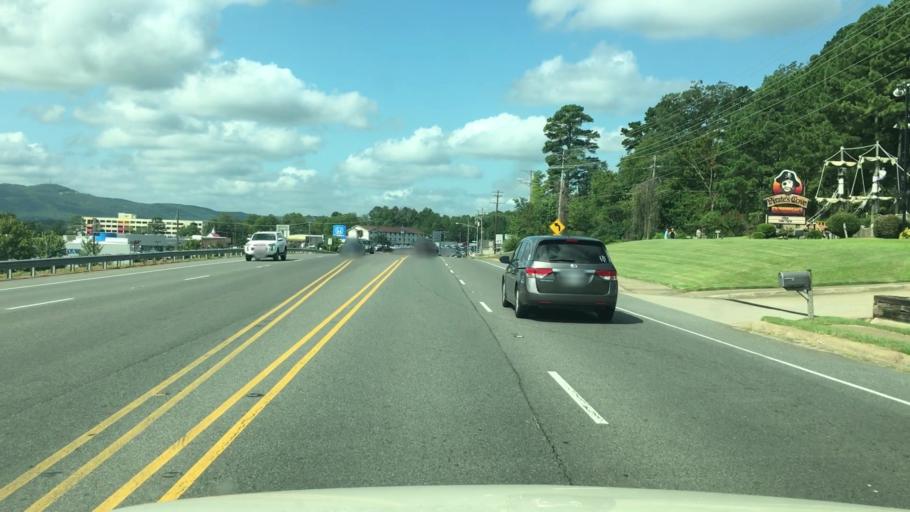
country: US
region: Arkansas
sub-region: Garland County
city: Lake Hamilton
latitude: 34.4483
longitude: -93.0865
